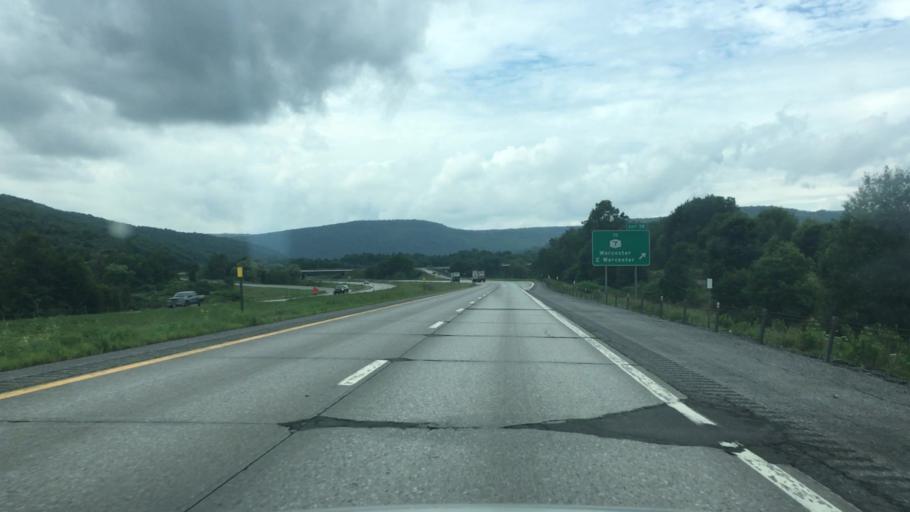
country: US
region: New York
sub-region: Otsego County
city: Worcester
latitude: 42.5945
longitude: -74.7205
